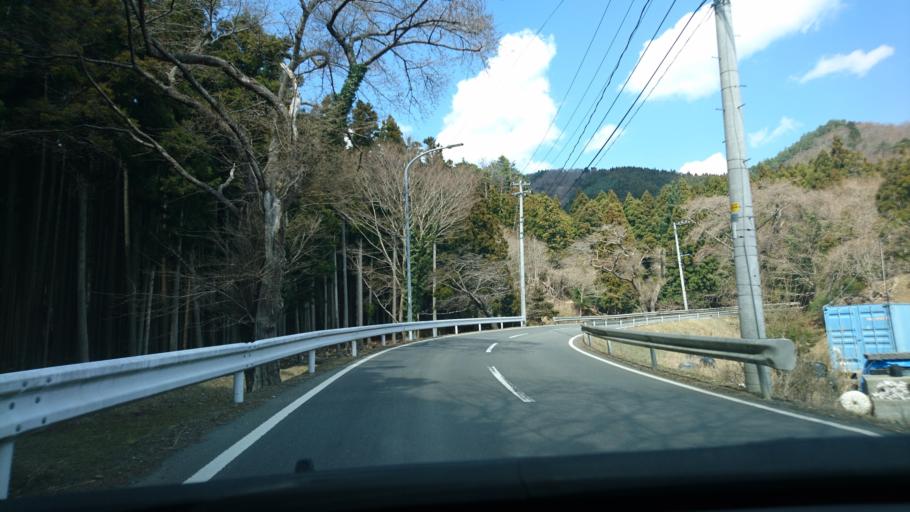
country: JP
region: Miyagi
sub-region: Oshika Gun
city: Onagawa Cho
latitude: 38.4724
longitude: 141.4848
